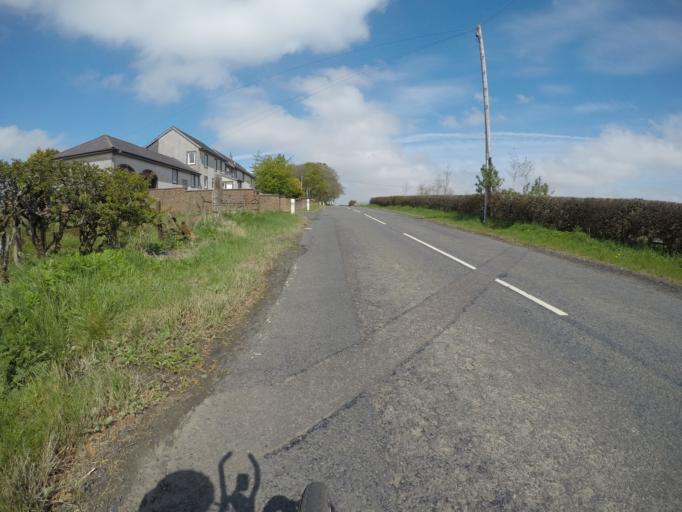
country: GB
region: Scotland
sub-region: East Ayrshire
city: Stewarton
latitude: 55.6983
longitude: -4.4858
